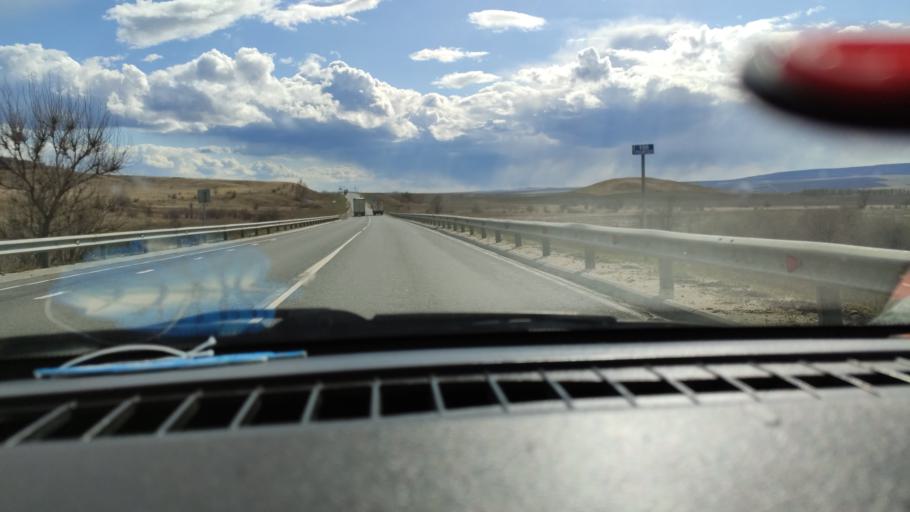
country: RU
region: Saratov
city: Alekseyevka
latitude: 52.3493
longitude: 47.9393
